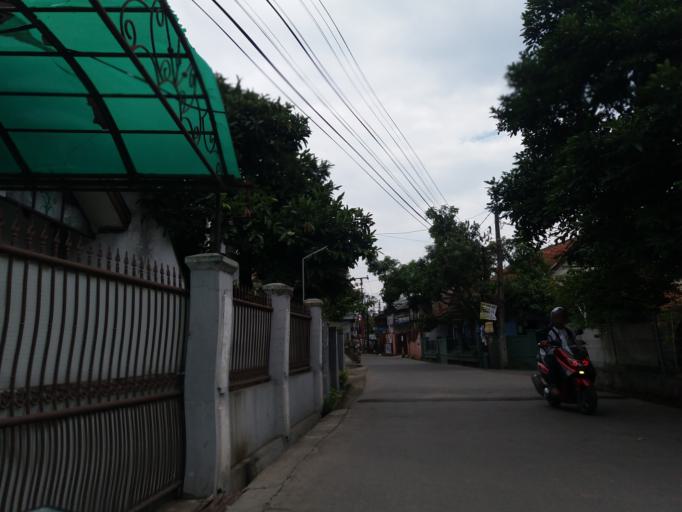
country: ID
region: West Java
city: Bandung
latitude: -6.9230
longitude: 107.6539
